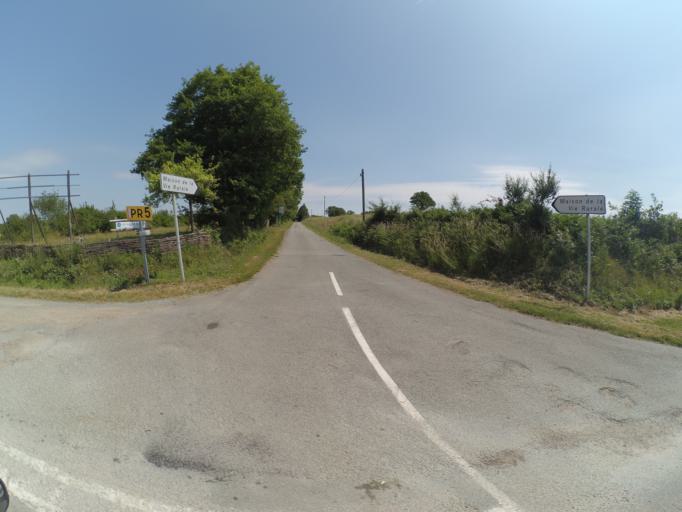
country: FR
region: Pays de la Loire
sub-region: Departement de la Vendee
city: La Flocelliere
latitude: 46.8132
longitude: -0.8640
